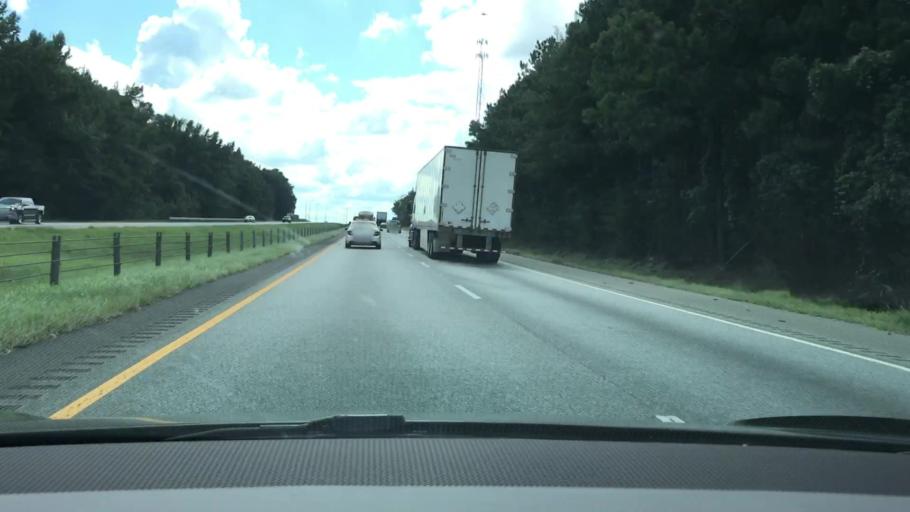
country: US
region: Alabama
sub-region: Lee County
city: Auburn
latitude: 32.5648
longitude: -85.4962
